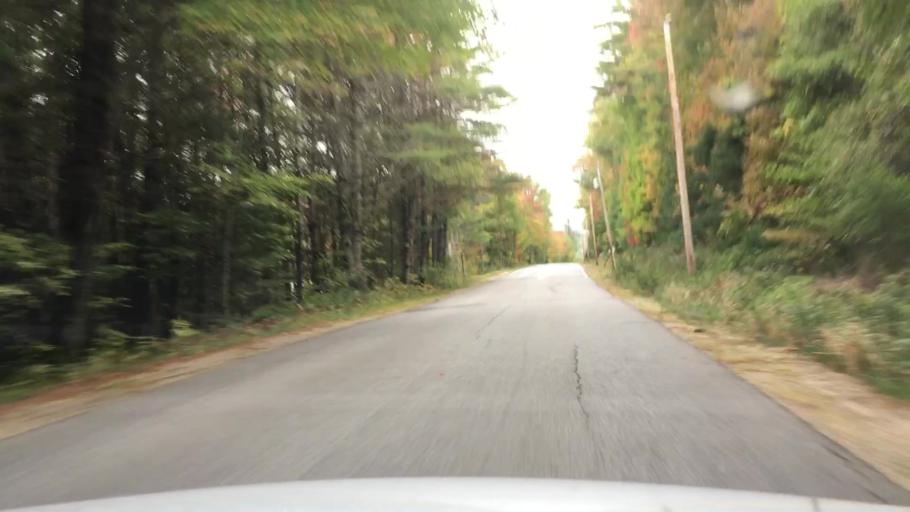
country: US
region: Maine
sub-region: Cumberland County
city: Harrison
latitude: 44.2585
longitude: -70.7254
